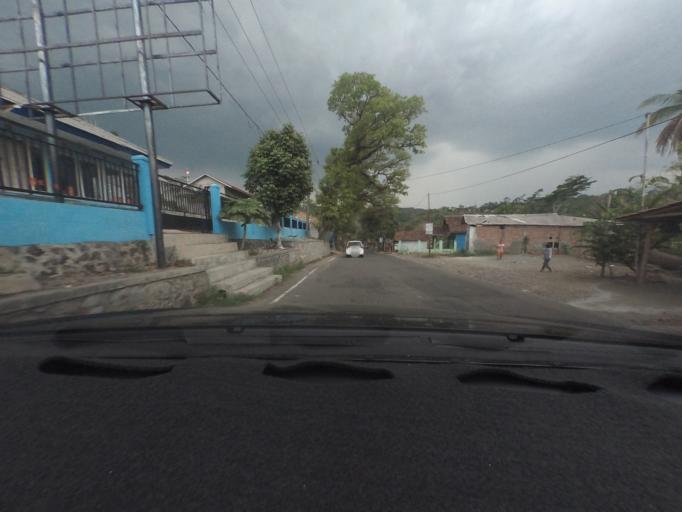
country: ID
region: West Java
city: Sindangsari
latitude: -6.9926
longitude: 106.6701
